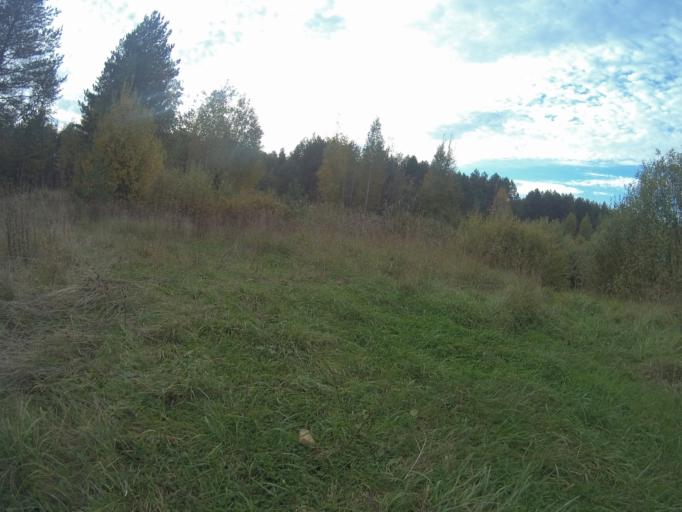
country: RU
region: Vladimir
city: Golovino
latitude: 55.9647
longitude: 40.4199
